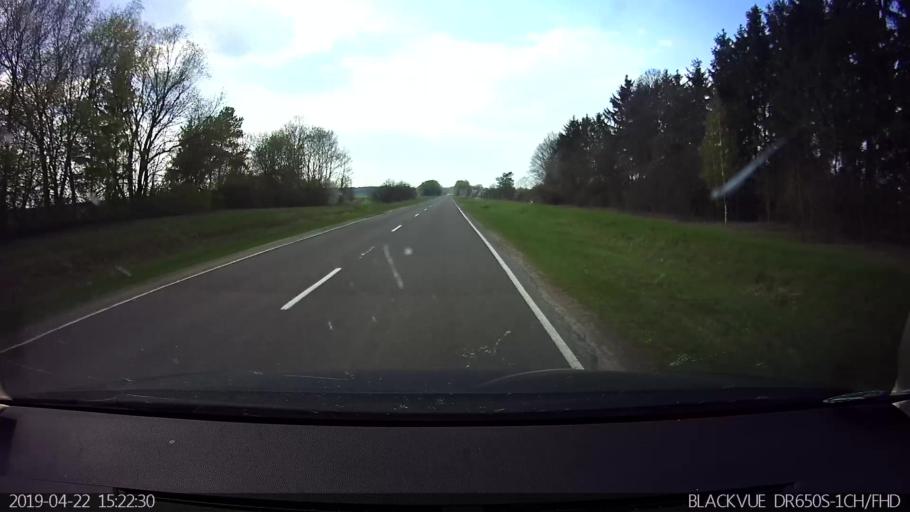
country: BY
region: Brest
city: Vysokaye
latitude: 52.3503
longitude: 23.4444
